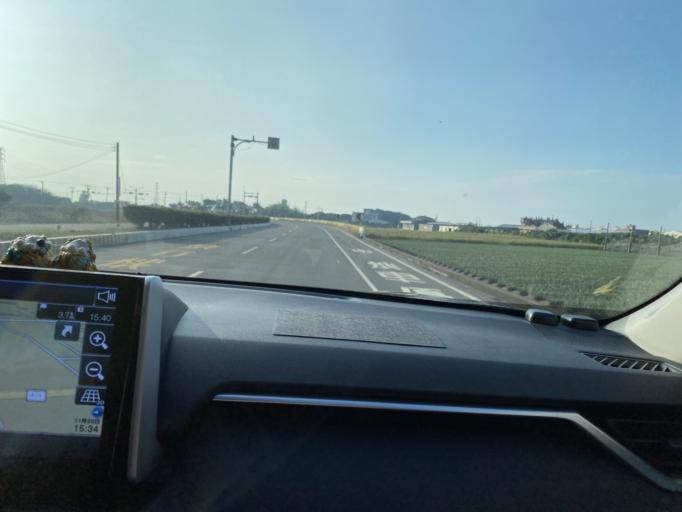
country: TW
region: Taiwan
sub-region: Changhua
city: Chang-hua
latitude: 23.9627
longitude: 120.3746
